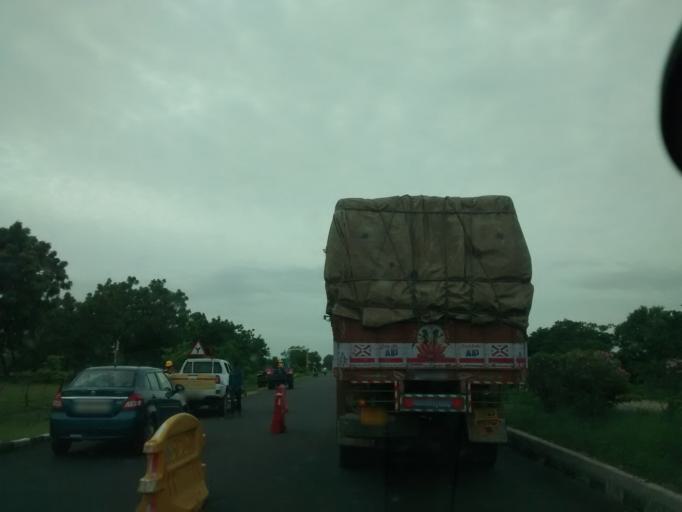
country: IN
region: Telangana
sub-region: Mahbubnagar
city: Wanparti
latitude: 16.3536
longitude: 77.9467
